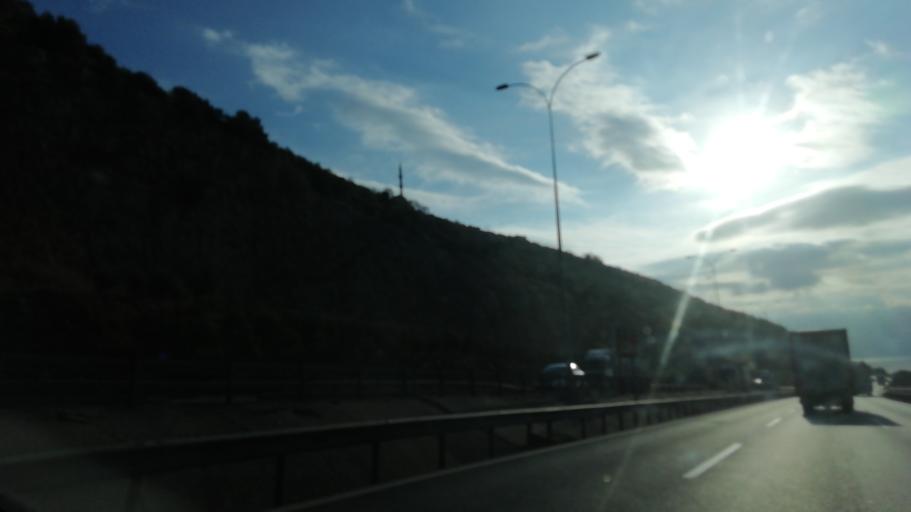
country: TR
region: Kocaeli
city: Hereke
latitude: 40.7831
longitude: 29.6263
